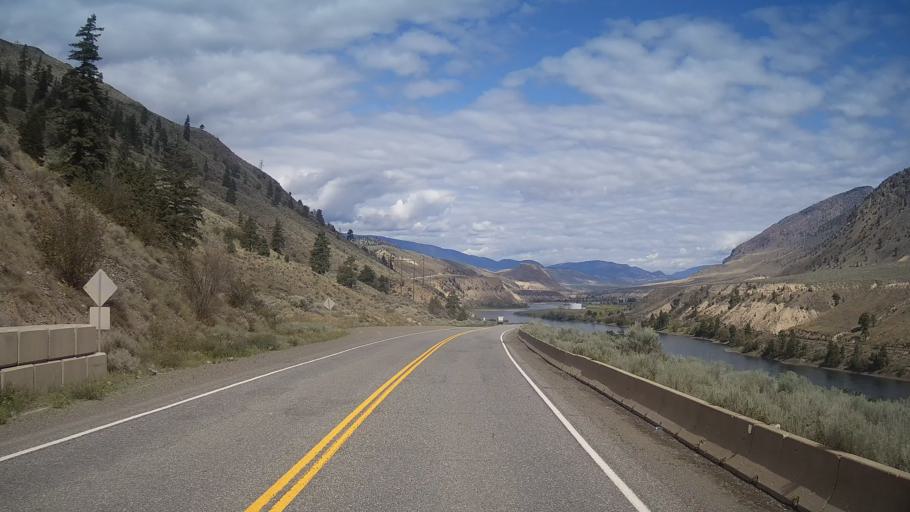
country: CA
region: British Columbia
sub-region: Thompson-Nicola Regional District
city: Ashcroft
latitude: 50.5413
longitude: -121.2893
